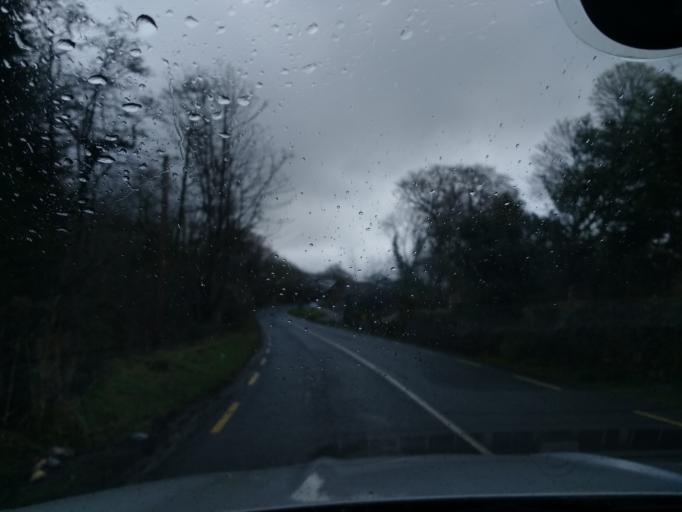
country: IE
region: Ulster
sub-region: County Donegal
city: Ramelton
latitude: 55.0763
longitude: -7.5926
